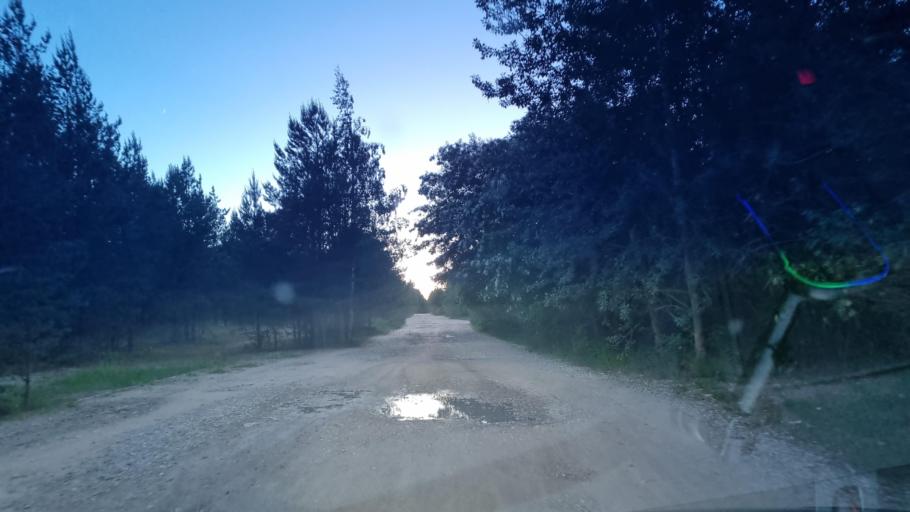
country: LV
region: Riga
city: Bolderaja
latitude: 57.0200
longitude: 24.0355
